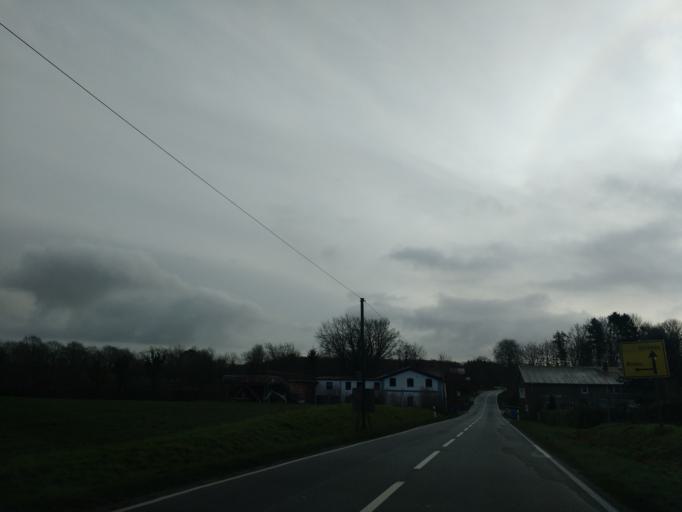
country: DE
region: Schleswig-Holstein
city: Damsdorf
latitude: 54.0589
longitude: 10.3314
